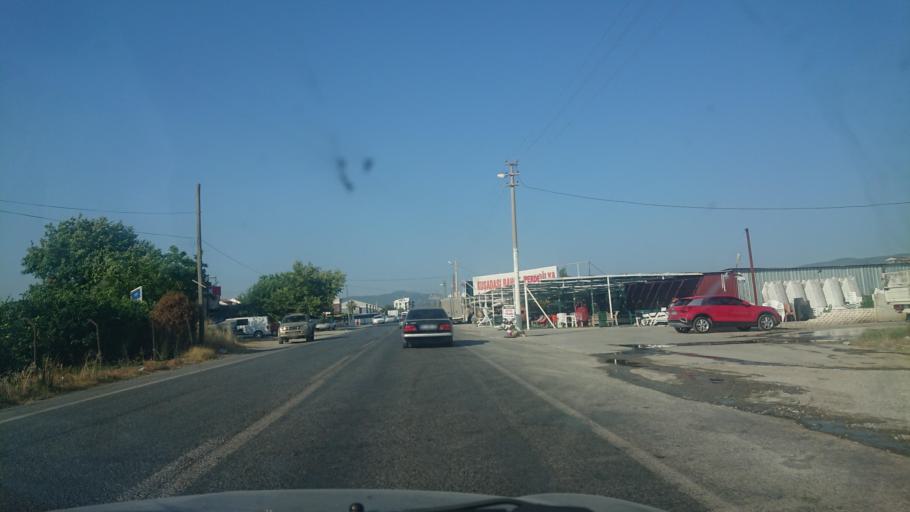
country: TR
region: Aydin
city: Davutlar
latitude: 37.7299
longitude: 27.2700
